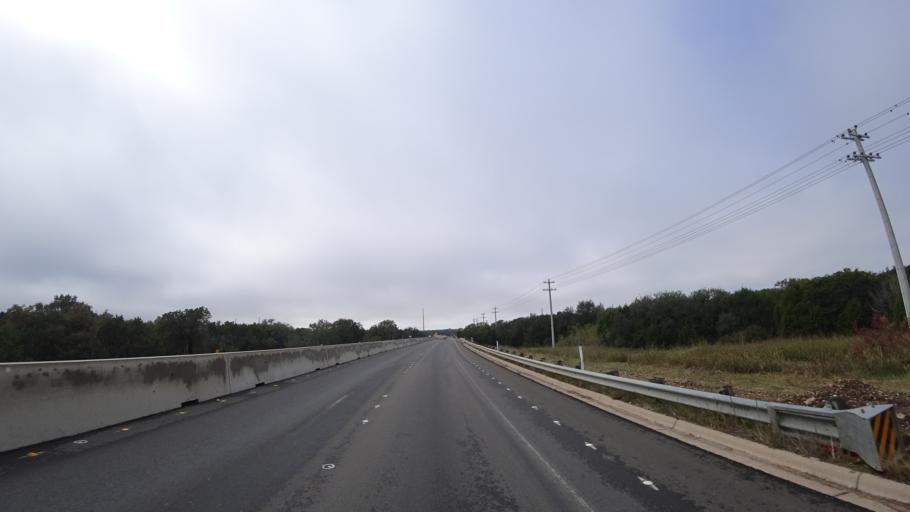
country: US
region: Texas
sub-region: Travis County
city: Shady Hollow
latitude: 30.1783
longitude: -97.8846
